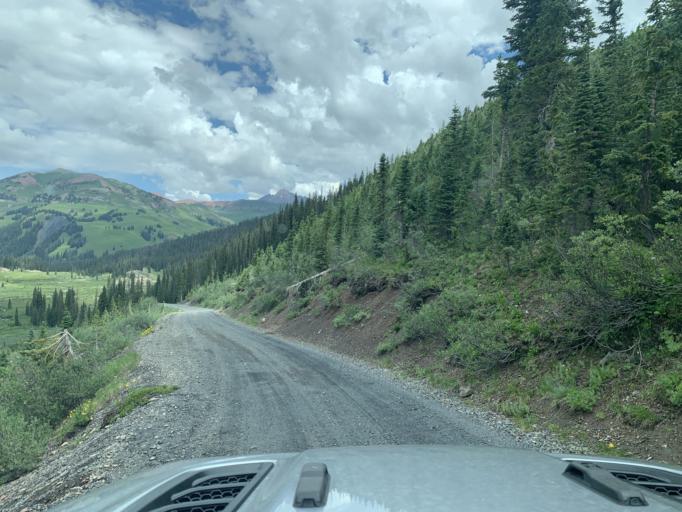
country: US
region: Colorado
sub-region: Gunnison County
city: Crested Butte
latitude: 39.0062
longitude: -107.0558
